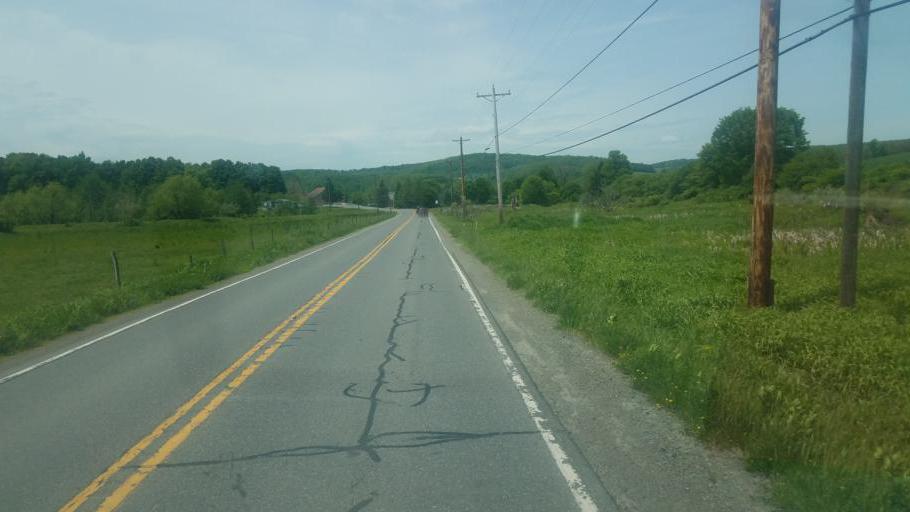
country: US
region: Pennsylvania
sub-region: Tioga County
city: Wellsboro
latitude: 41.7705
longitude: -77.2367
